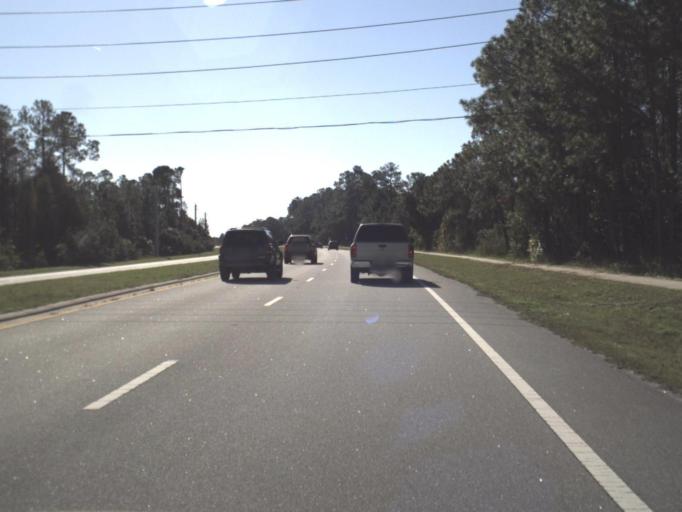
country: US
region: Florida
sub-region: Volusia County
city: Ormond Beach
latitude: 29.2445
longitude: -81.0936
